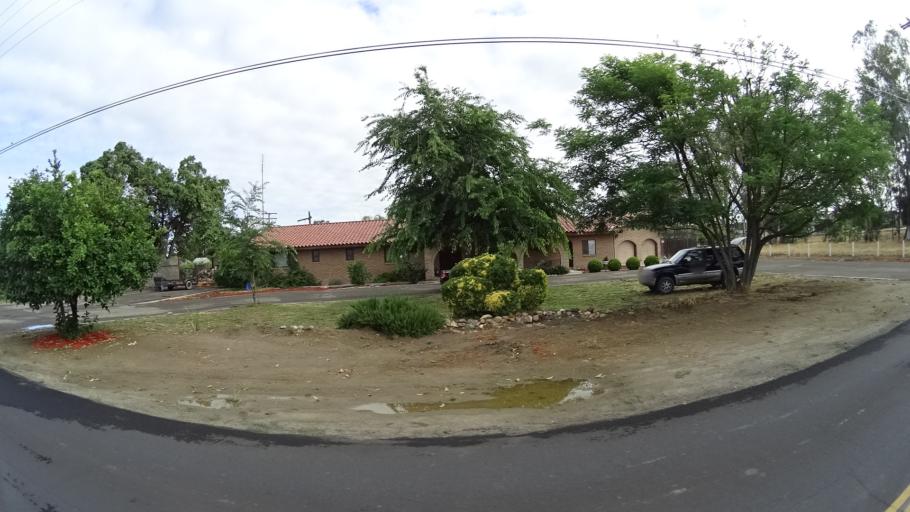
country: US
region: California
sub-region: Kings County
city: Hanford
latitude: 36.3572
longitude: -119.6278
